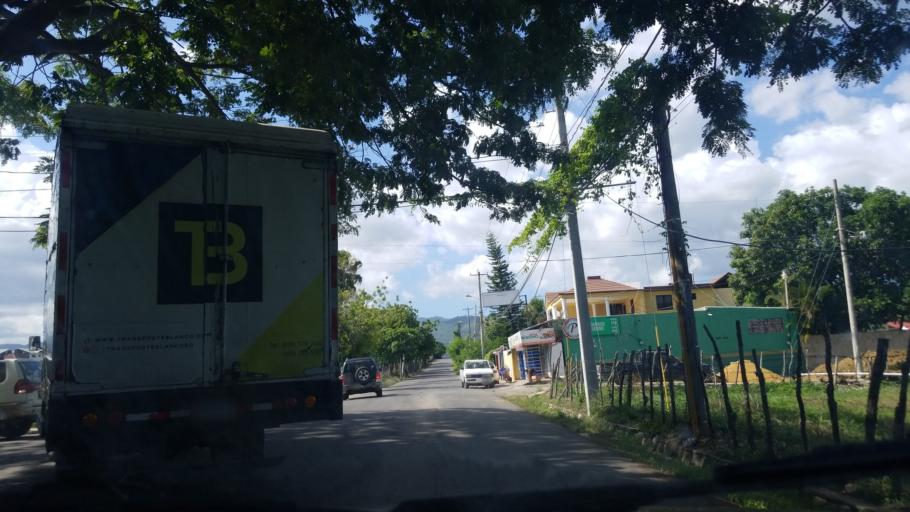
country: DO
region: Santiago
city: Santiago de los Caballeros
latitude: 19.4853
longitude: -70.6871
